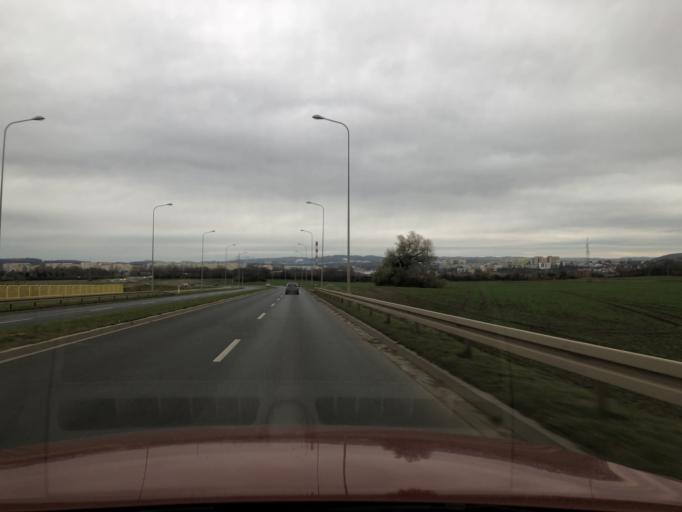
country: PL
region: Lower Silesian Voivodeship
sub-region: Powiat walbrzyski
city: Szczawno-Zdroj
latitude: 50.8167
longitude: 16.2454
